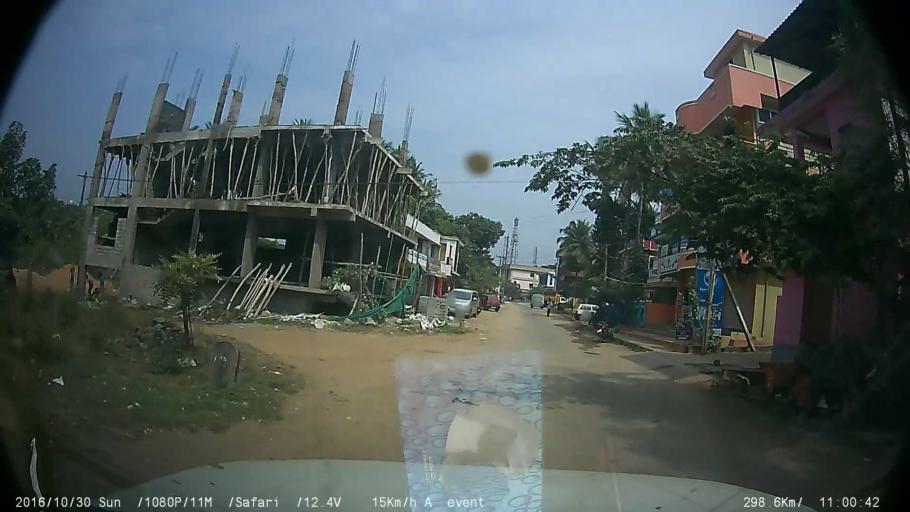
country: IN
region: Karnataka
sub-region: Kodagu
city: Kushalnagar
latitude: 12.4542
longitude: 75.9609
